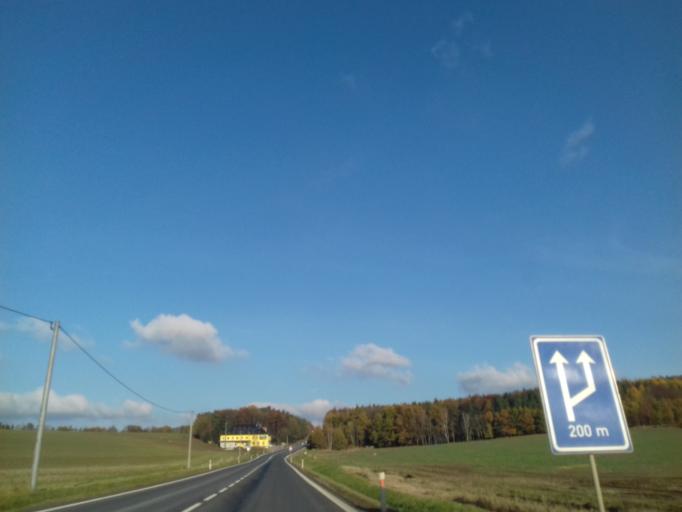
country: CZ
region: Plzensky
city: Holysov
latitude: 49.6001
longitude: 13.1092
